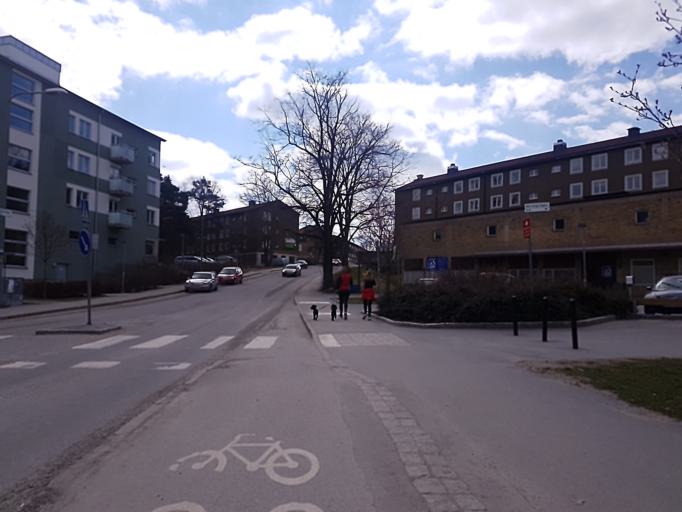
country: SE
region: Stockholm
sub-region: Nacka Kommun
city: Nacka
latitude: 59.2867
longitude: 18.1182
